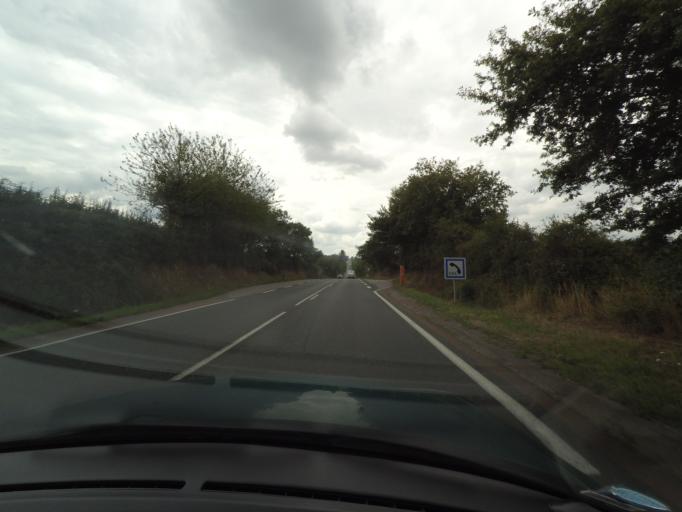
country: FR
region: Poitou-Charentes
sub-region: Departement des Deux-Sevres
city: Chatillon-sur-Thouet
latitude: 46.6480
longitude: -0.2004
